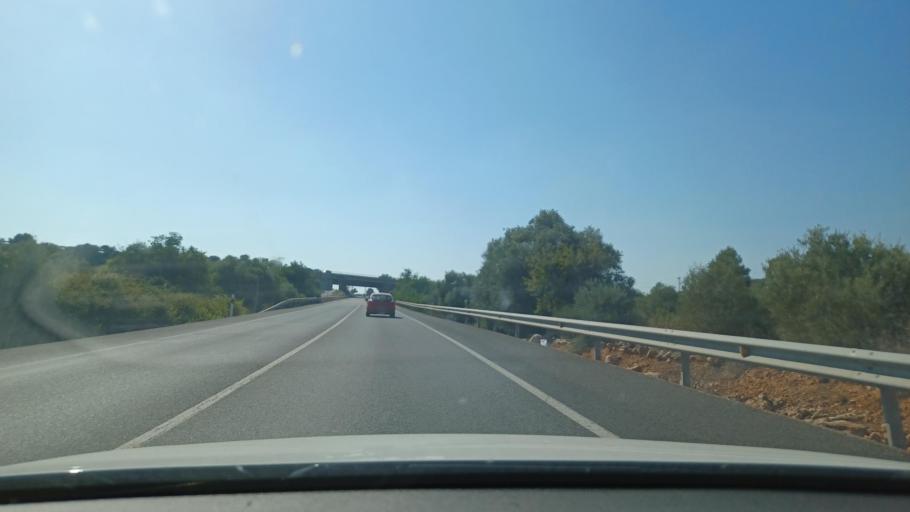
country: ES
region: Valencia
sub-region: Provincia de Castello
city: Alcala de Xivert
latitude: 40.2736
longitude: 0.2374
